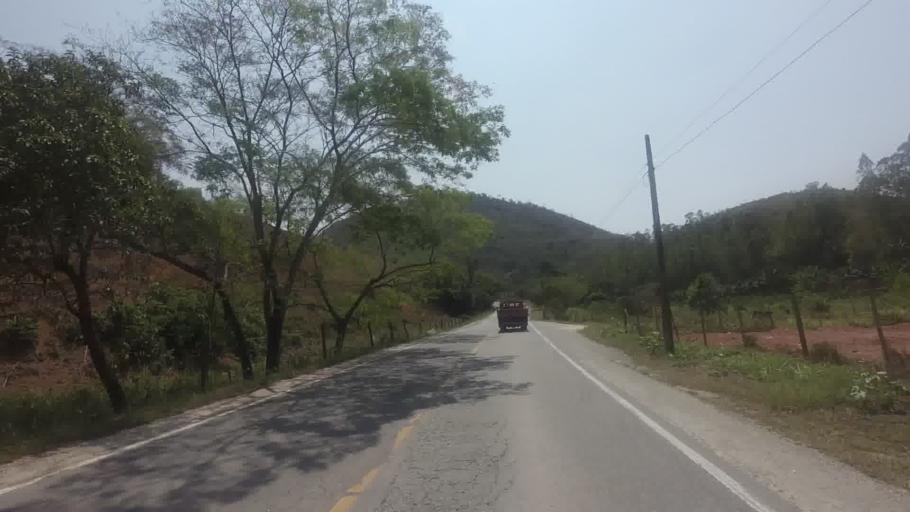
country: BR
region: Espirito Santo
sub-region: Cachoeiro De Itapemirim
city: Cachoeiro de Itapemirim
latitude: -20.8658
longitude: -41.0379
